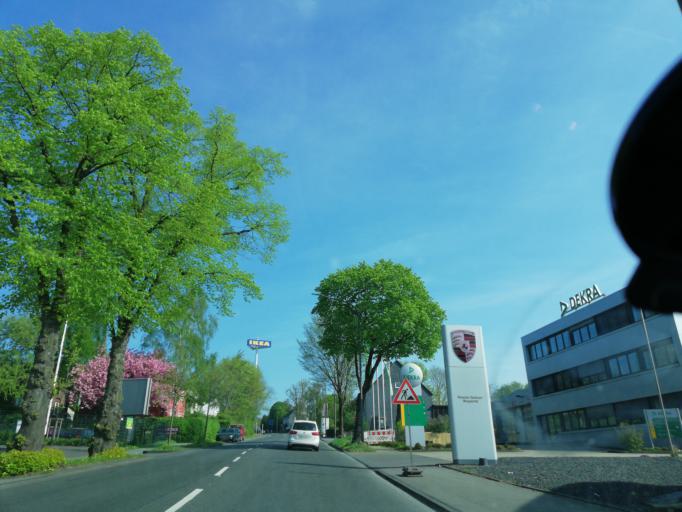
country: DE
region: North Rhine-Westphalia
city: Sprockhovel
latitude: 51.3054
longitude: 7.2523
